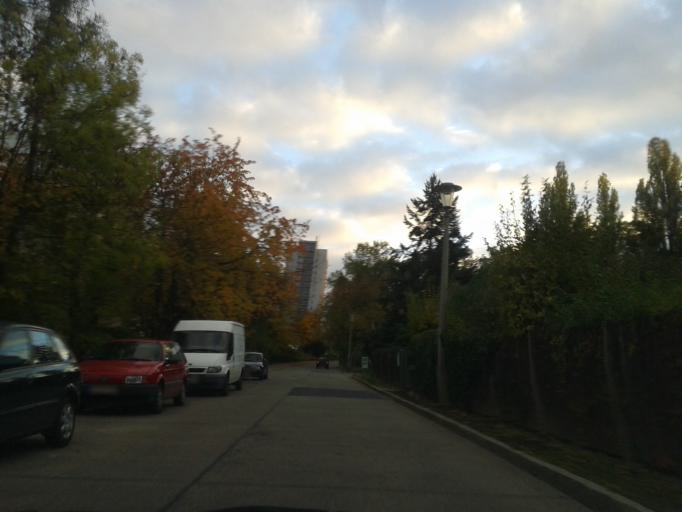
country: DE
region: Saxony
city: Dresden
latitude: 51.0258
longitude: 13.7422
